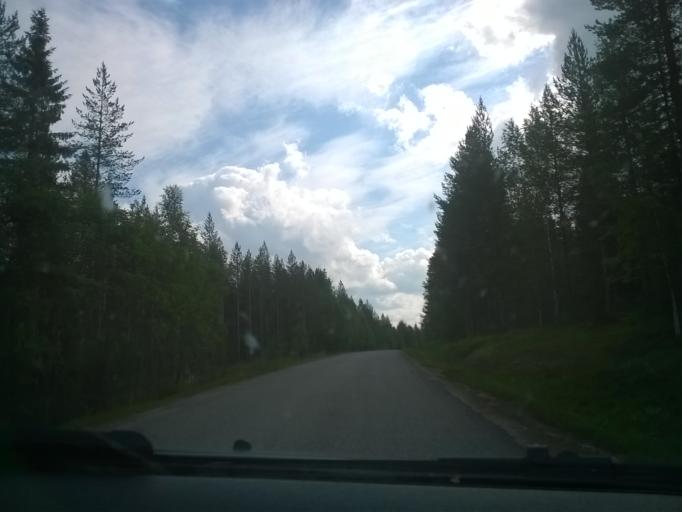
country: FI
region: Kainuu
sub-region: Kehys-Kainuu
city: Kuhmo
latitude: 64.4485
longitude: 29.6914
